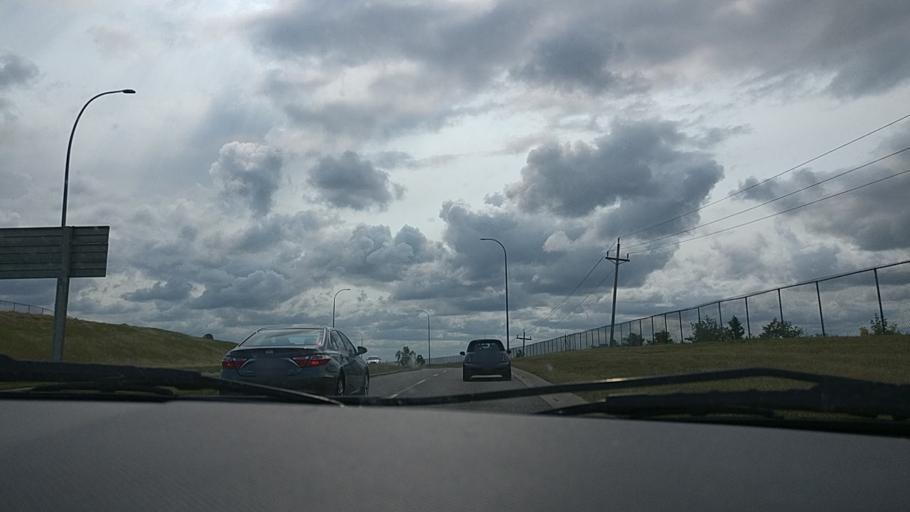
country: CA
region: Alberta
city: Calgary
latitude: 51.0952
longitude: -114.1141
